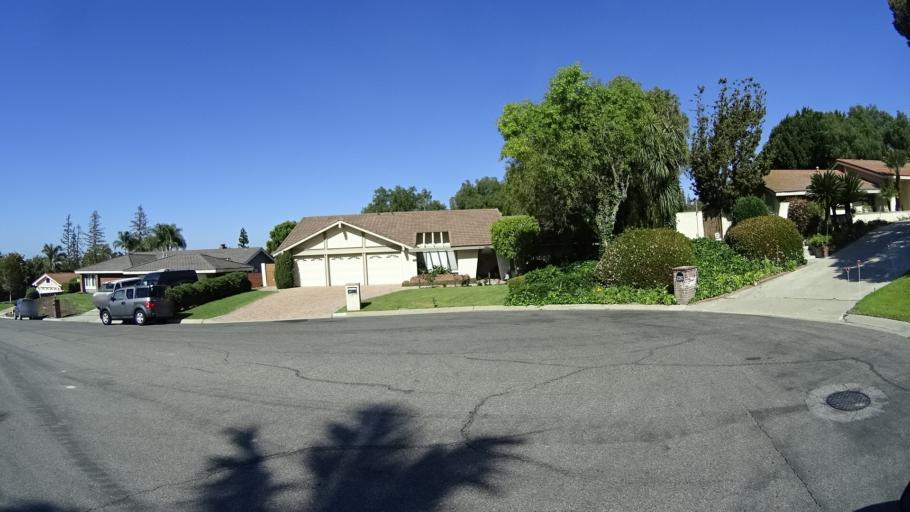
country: US
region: California
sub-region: Orange County
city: Villa Park
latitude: 33.8252
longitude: -117.8198
